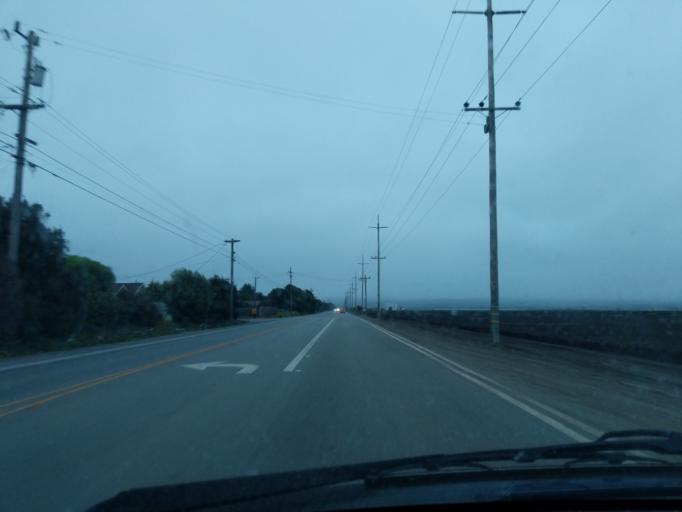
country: US
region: California
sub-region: Monterey County
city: Salinas
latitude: 36.6750
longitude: -121.6781
